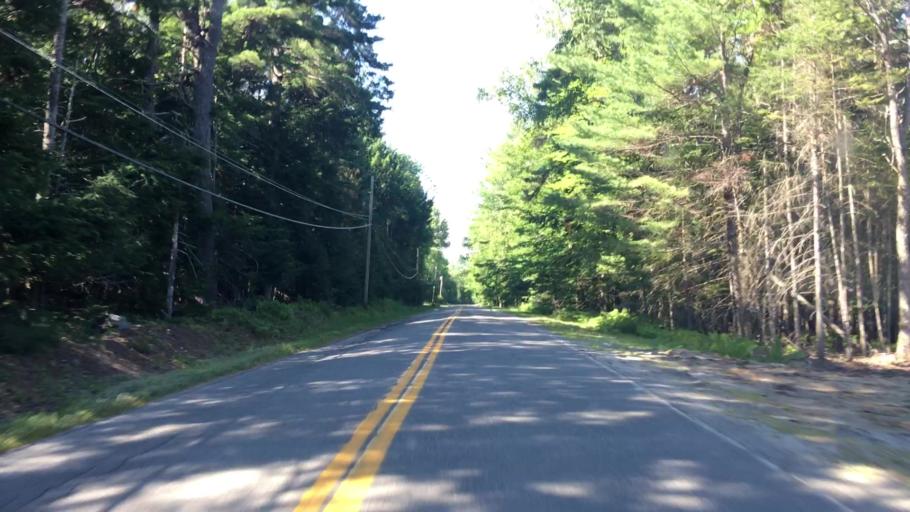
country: US
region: Maine
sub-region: Penobscot County
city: Enfield
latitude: 45.2649
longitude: -68.5623
